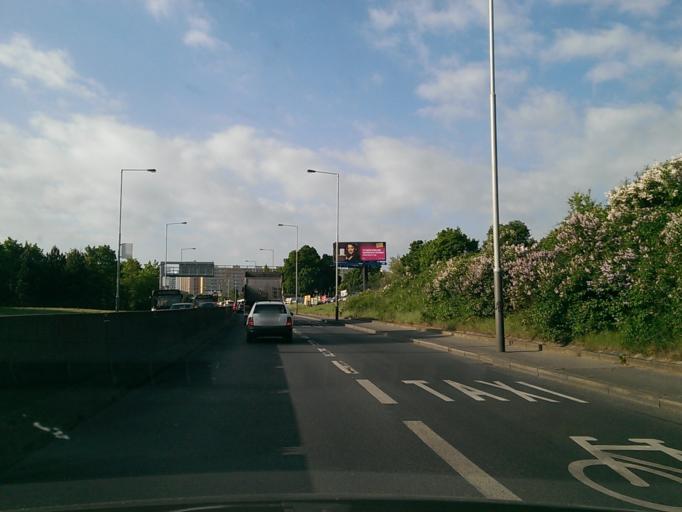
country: CZ
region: Praha
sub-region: Praha 4
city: Hodkovicky
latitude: 50.0332
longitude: 14.4552
